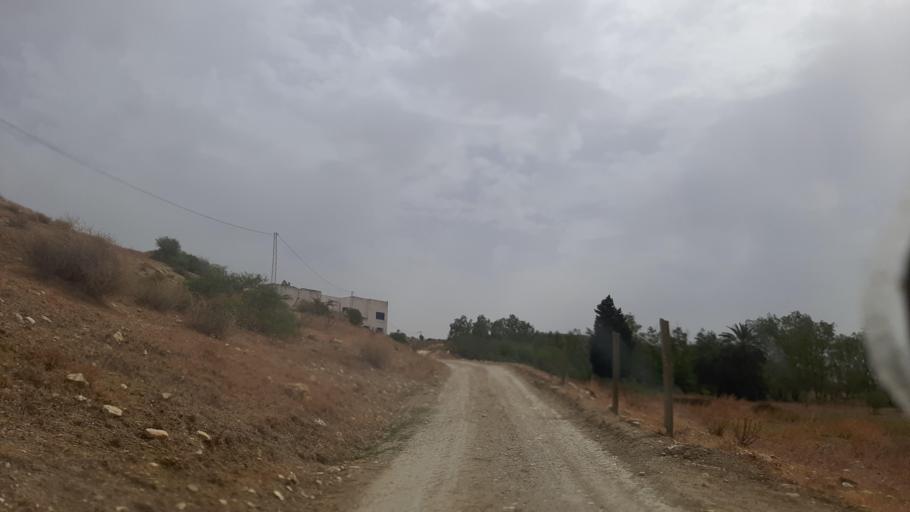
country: TN
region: Tunis
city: La Mohammedia
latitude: 36.5697
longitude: 10.1380
